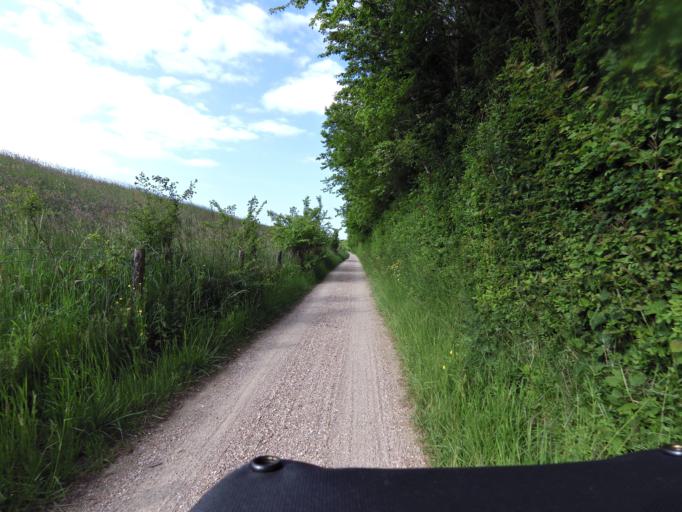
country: NL
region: Zeeland
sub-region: Schouwen-Duiveland
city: Renesse
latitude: 51.6954
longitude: 3.7919
